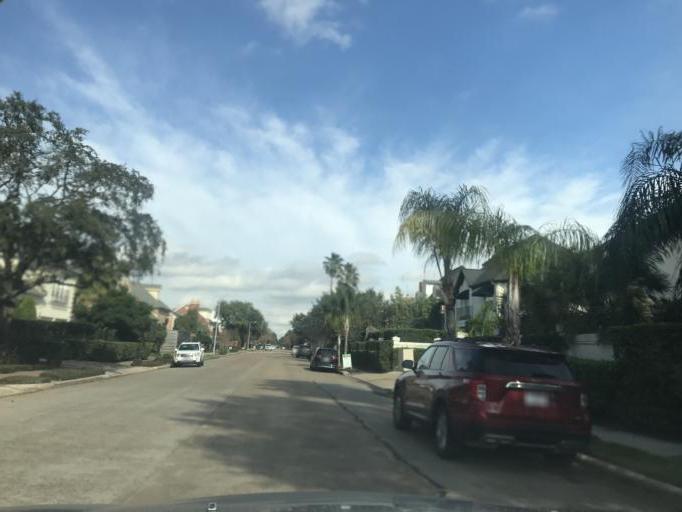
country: US
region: Texas
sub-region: Harris County
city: Hunters Creek Village
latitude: 29.7437
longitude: -95.4887
